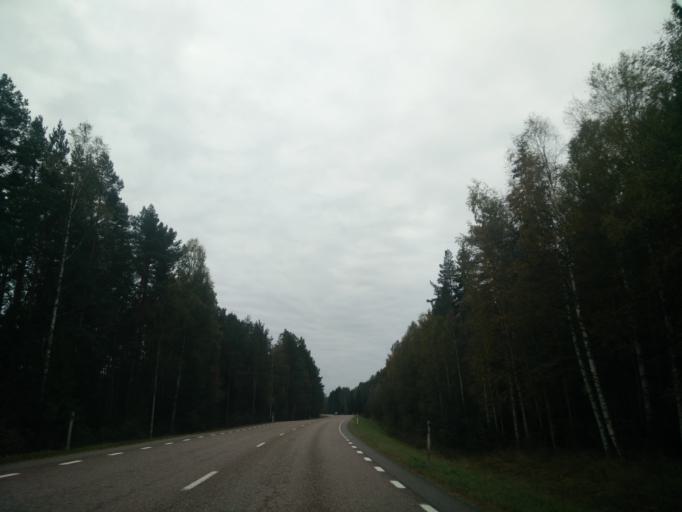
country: SE
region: Gaevleborg
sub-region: Gavle Kommun
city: Norrsundet
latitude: 60.8468
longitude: 17.1979
